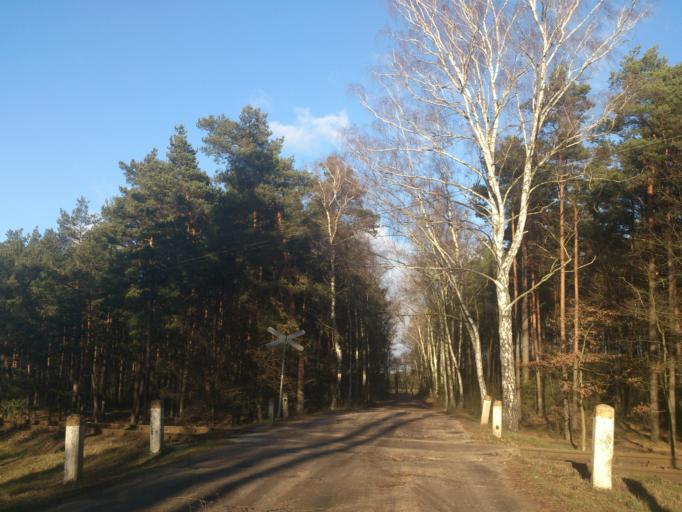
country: PL
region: Kujawsko-Pomorskie
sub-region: Powiat torunski
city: Lubicz Gorny
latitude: 53.0123
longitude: 18.7983
